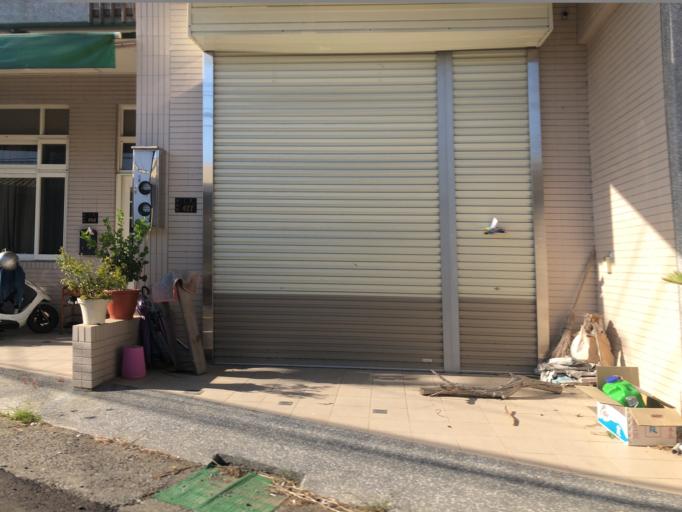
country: TW
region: Taiwan
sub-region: Hsinchu
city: Hsinchu
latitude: 24.7361
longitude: 120.9701
